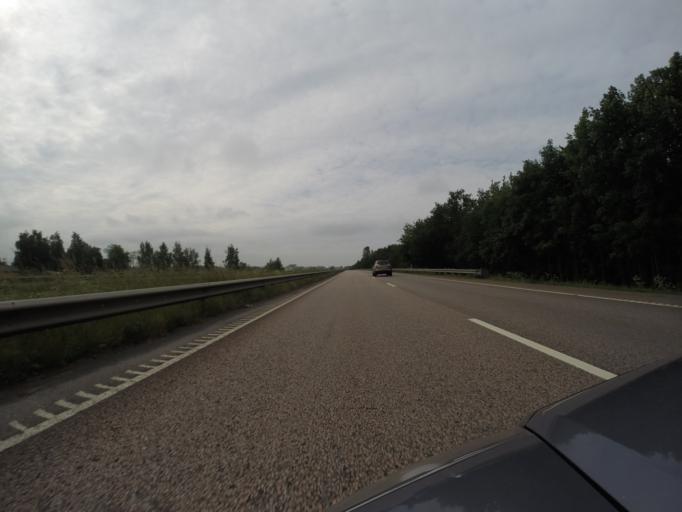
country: SE
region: Skane
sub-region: Helsingborg
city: Gantofta
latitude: 56.0100
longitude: 12.7799
